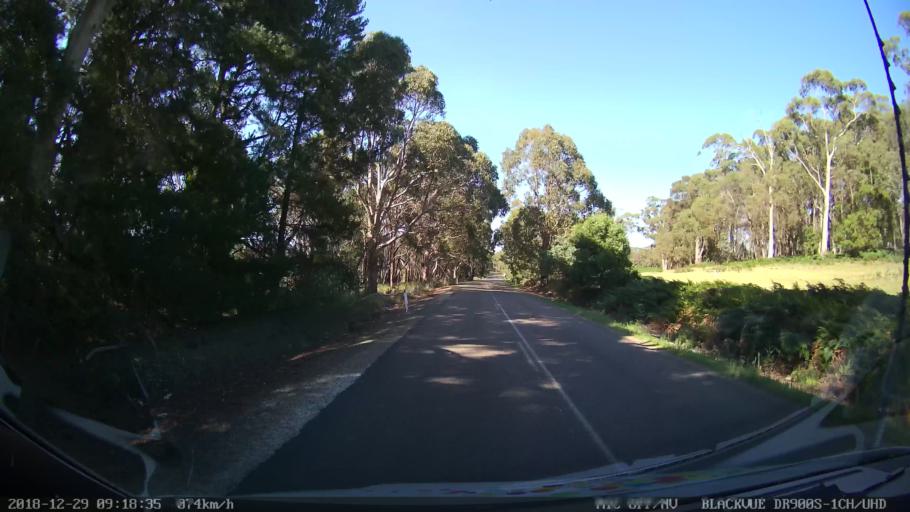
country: AU
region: New South Wales
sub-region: Upper Lachlan Shire
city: Crookwell
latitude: -34.4733
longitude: 149.4349
